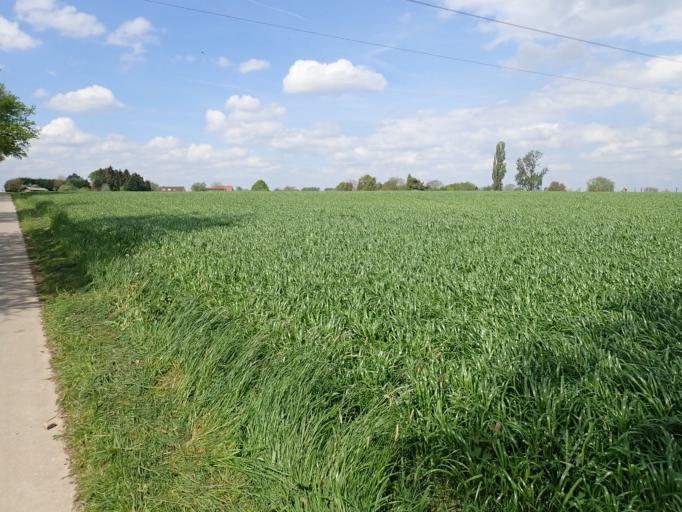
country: BE
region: Flanders
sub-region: Provincie Vlaams-Brabant
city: Opwijk
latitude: 50.9371
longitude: 4.1838
